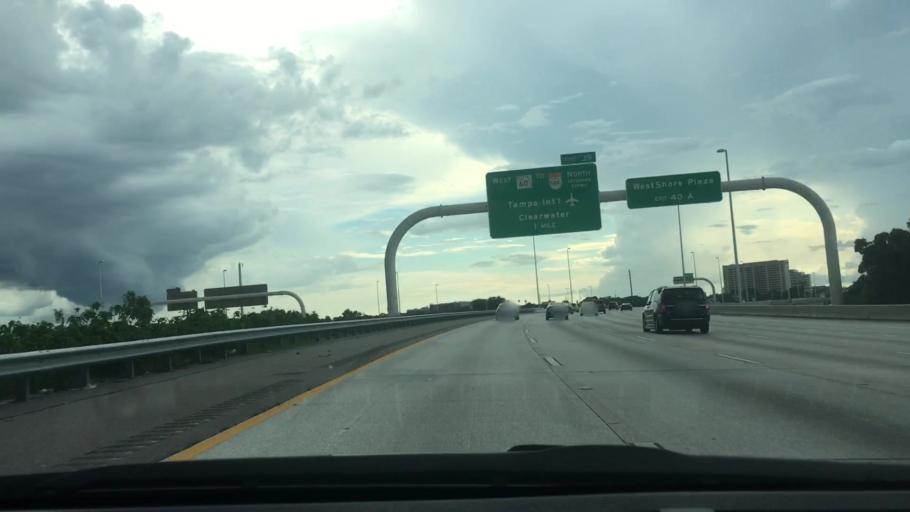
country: US
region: Florida
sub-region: Hillsborough County
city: Tampa
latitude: 27.9531
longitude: -82.5108
